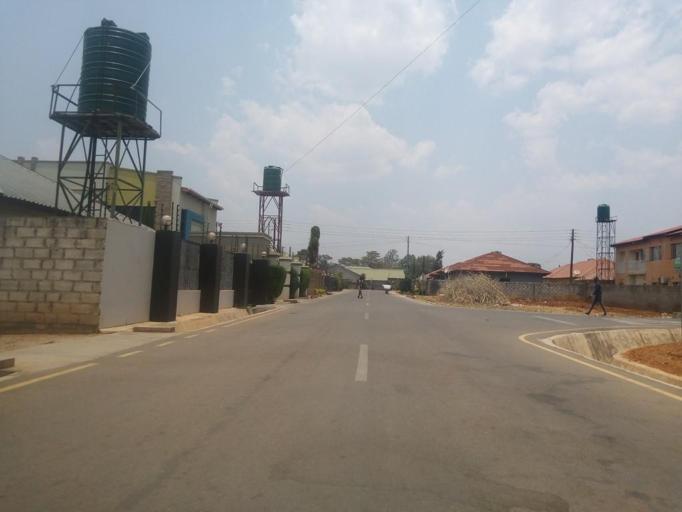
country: ZM
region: Lusaka
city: Lusaka
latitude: -15.3983
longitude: 28.3925
